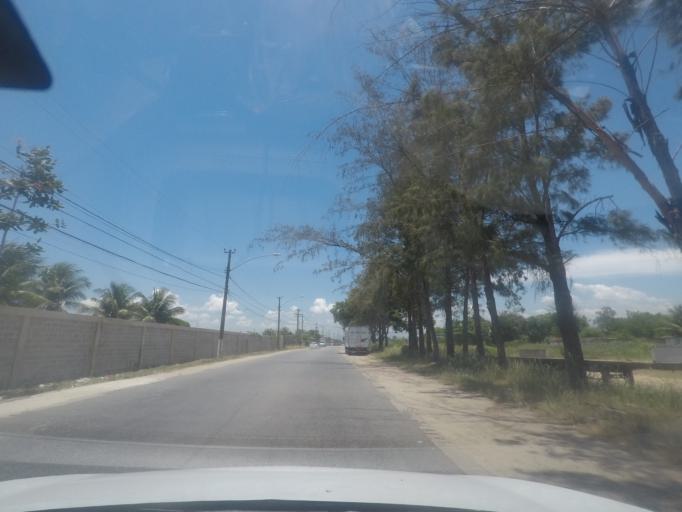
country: BR
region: Rio de Janeiro
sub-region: Itaguai
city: Itaguai
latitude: -22.9039
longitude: -43.6919
